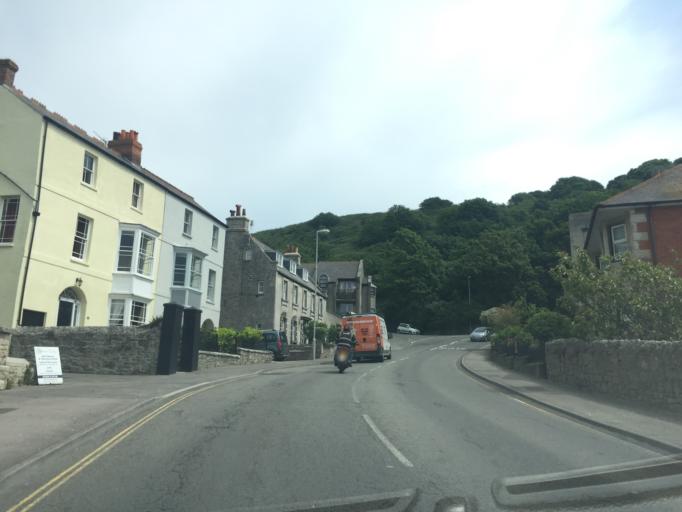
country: GB
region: England
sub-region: Dorset
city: Fortuneswell
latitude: 50.5587
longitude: -2.4409
